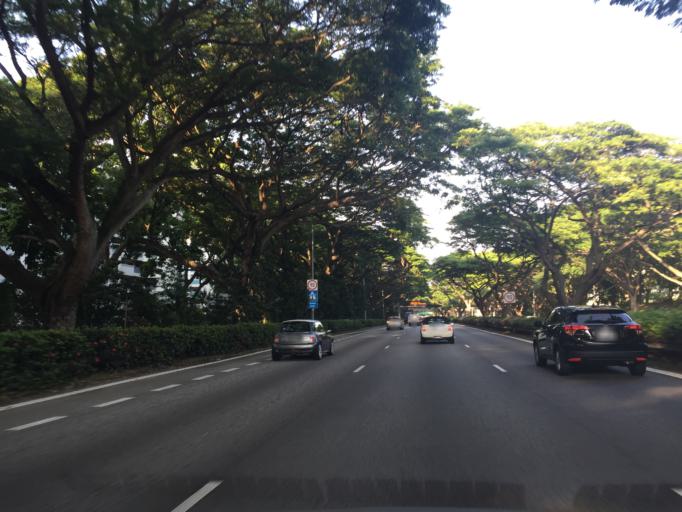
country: SG
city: Singapore
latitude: 1.3477
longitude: 103.9542
